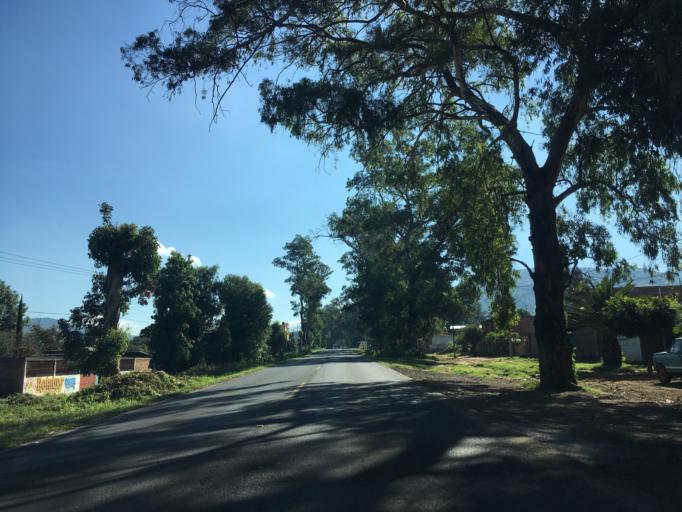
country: MX
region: Mexico
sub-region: Chalco
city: Zopoco
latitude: 19.8434
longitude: -102.0777
